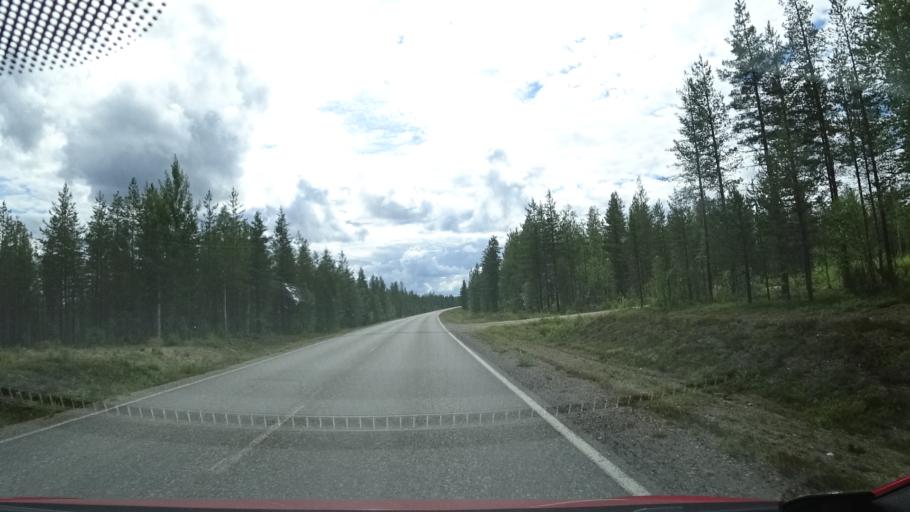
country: FI
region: Lapland
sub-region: Tunturi-Lappi
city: Kittilae
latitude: 67.5227
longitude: 24.9073
